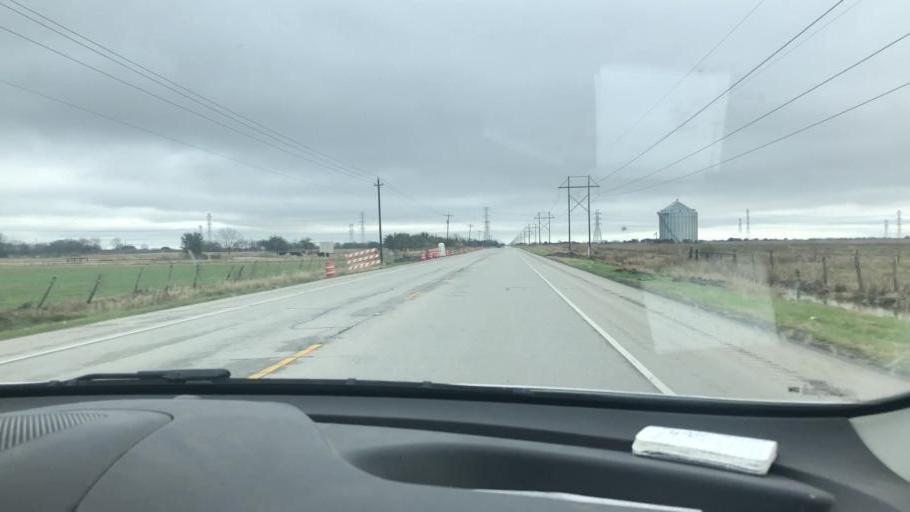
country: US
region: Texas
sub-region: Wharton County
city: Boling
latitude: 29.1801
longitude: -96.0080
